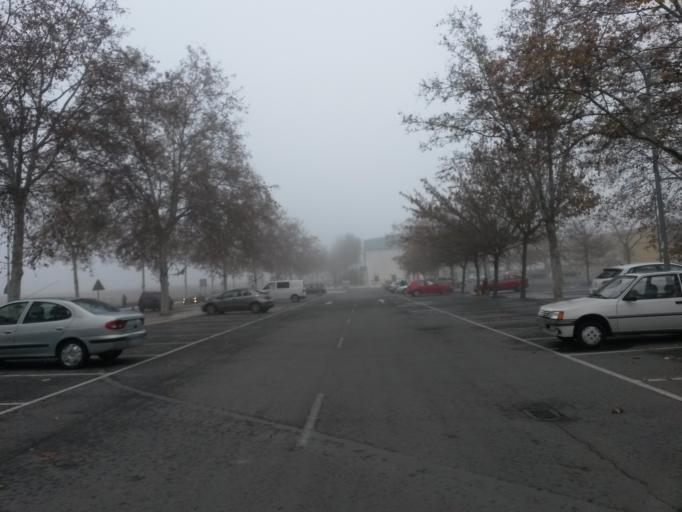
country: ES
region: Castille and Leon
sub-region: Provincia de Salamanca
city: Salamanca
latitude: 40.9816
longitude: -5.6545
